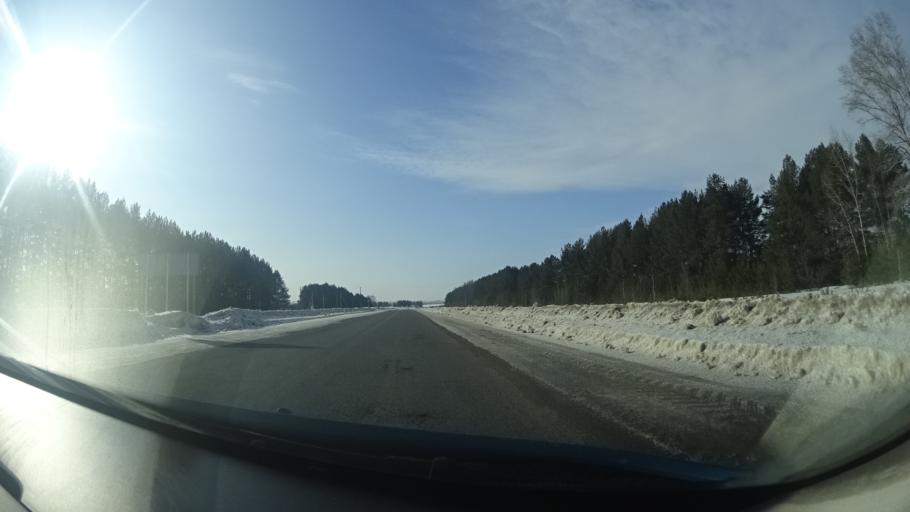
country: RU
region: Perm
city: Kuyeda
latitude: 56.4785
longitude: 55.5905
